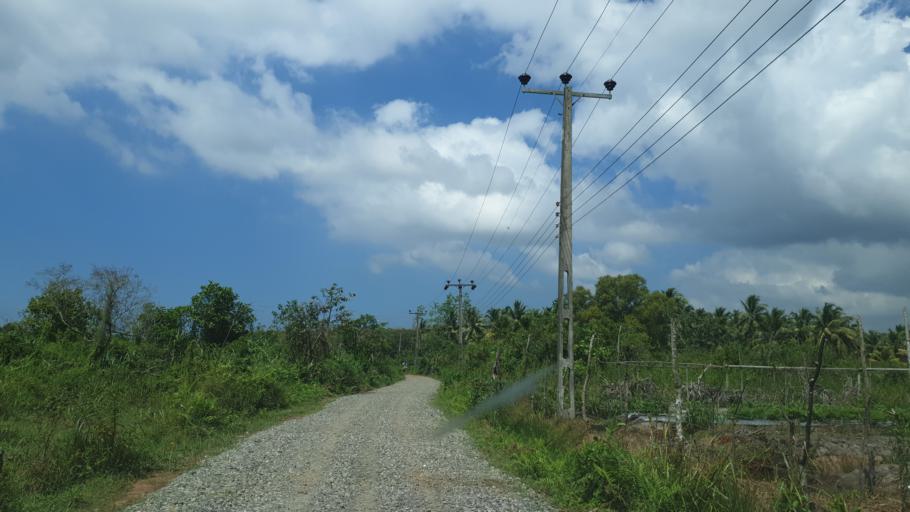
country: LK
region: Western
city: Panadura
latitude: 6.6770
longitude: 79.9623
